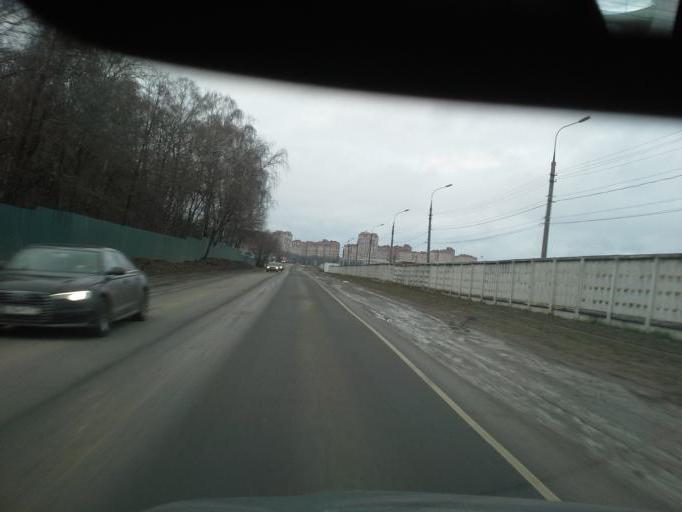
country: RU
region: Moskovskaya
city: Moskovskiy
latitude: 55.5861
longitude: 37.3559
